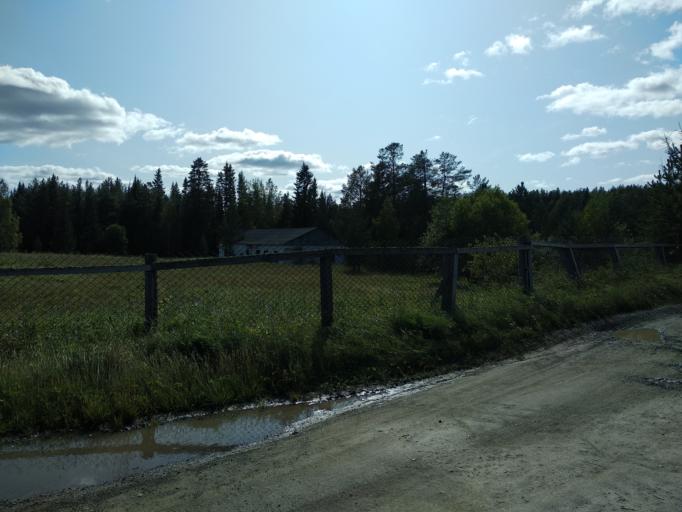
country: RU
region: Sverdlovsk
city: Karpinsk
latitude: 59.9048
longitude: 59.7459
